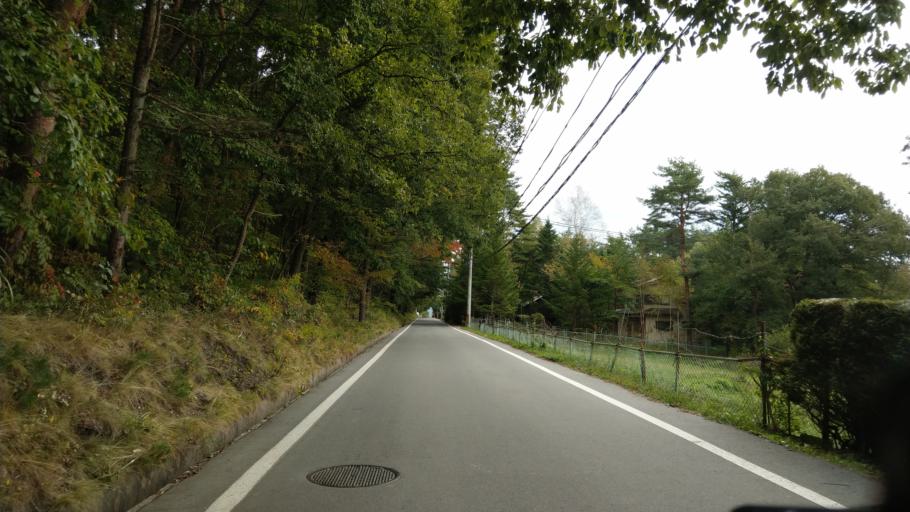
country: JP
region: Nagano
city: Komoro
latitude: 36.3265
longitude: 138.5251
